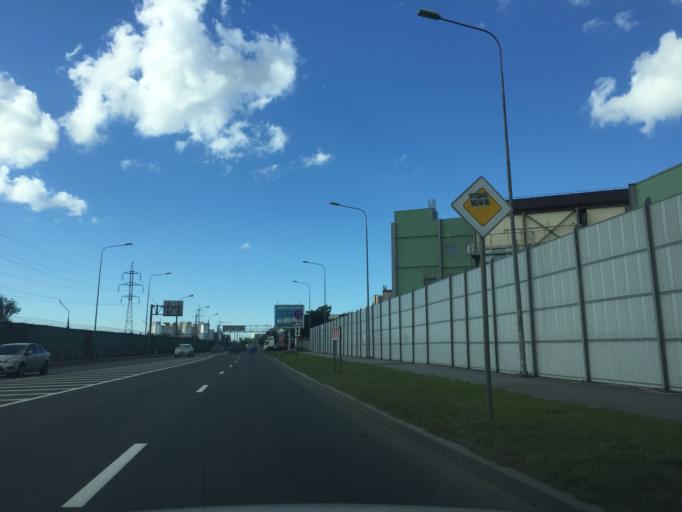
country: RU
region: St.-Petersburg
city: Dachnoye
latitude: 59.8353
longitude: 30.3063
